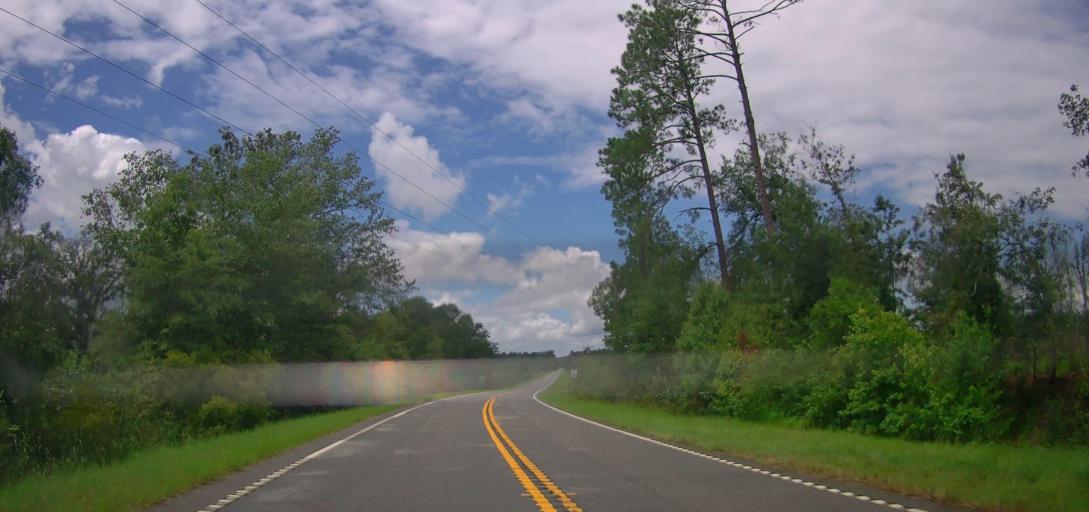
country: US
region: Georgia
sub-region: Wilcox County
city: Rochelle
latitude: 32.0364
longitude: -83.6102
